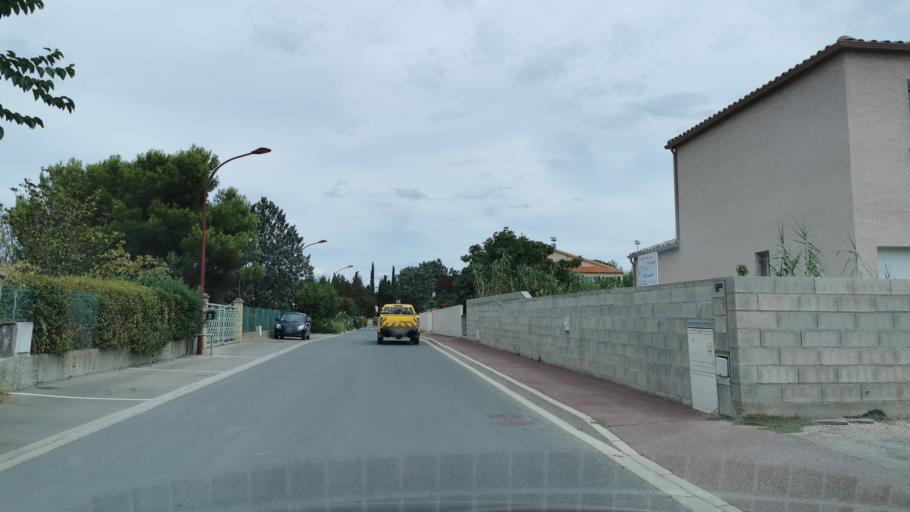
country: FR
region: Languedoc-Roussillon
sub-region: Departement de l'Aude
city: Argeliers
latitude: 43.3082
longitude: 2.9049
